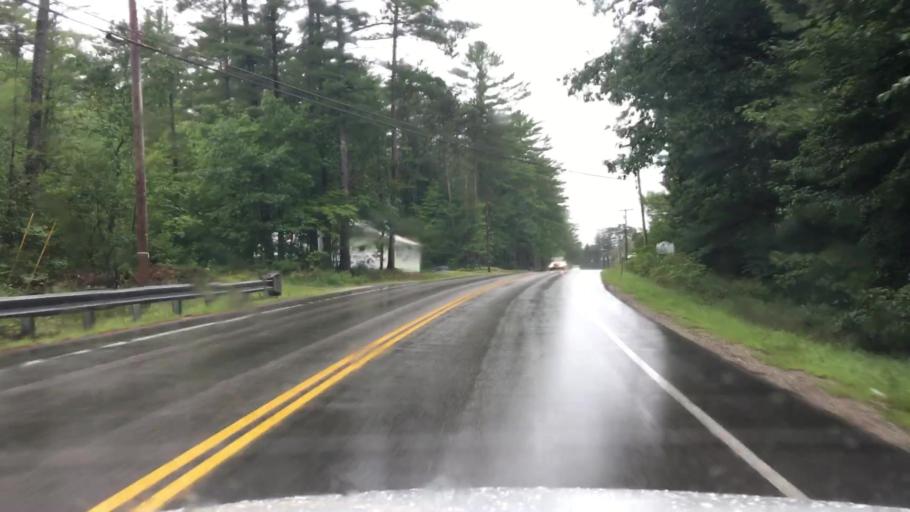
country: US
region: New Hampshire
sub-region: Carroll County
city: Conway
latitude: 43.9923
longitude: -71.0508
